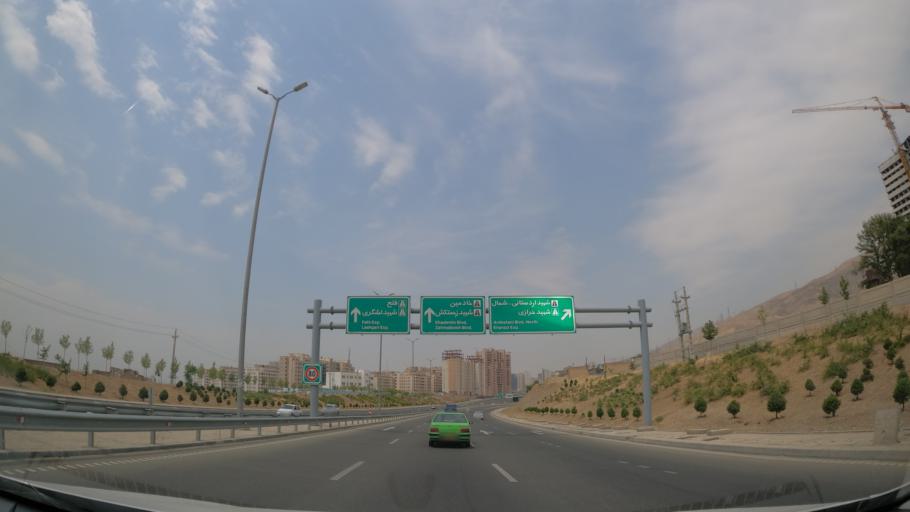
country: IR
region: Tehran
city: Shahr-e Qods
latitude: 35.7513
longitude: 51.1624
